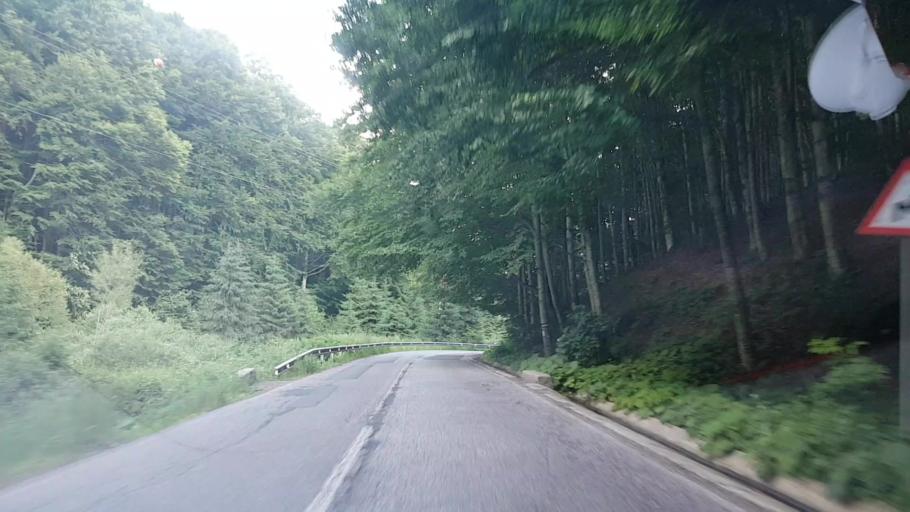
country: RO
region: Harghita
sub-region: Comuna Praid
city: Ocna de Sus
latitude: 46.5959
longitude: 25.2408
